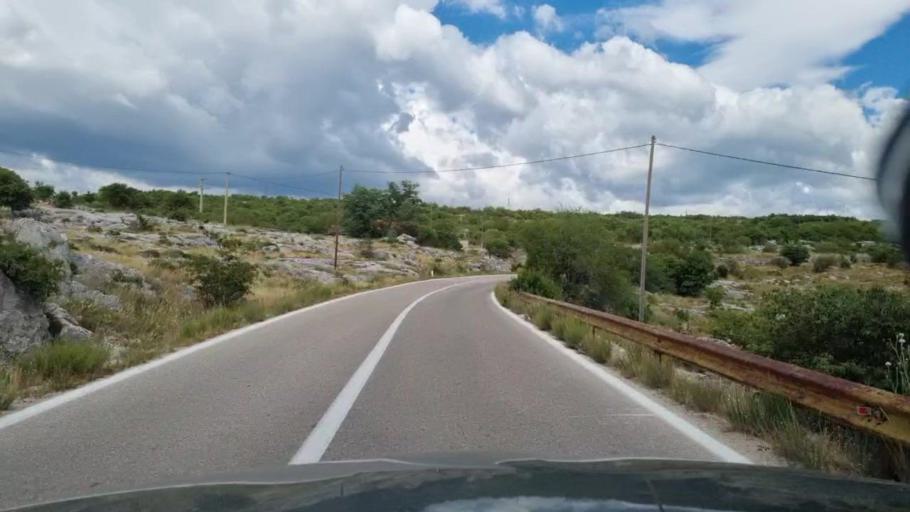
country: BA
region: Federation of Bosnia and Herzegovina
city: Blagaj
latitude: 43.2509
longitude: 17.9580
